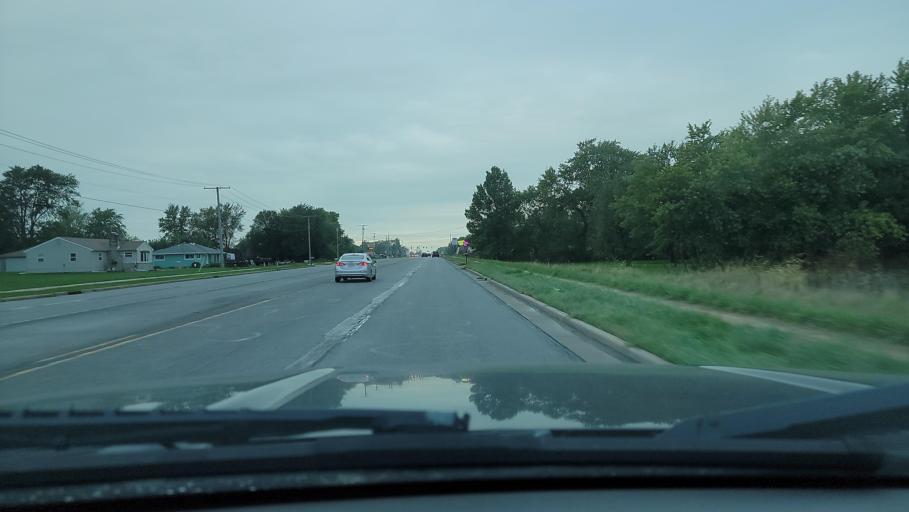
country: US
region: Indiana
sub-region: Porter County
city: South Haven
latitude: 41.5505
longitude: -87.1481
